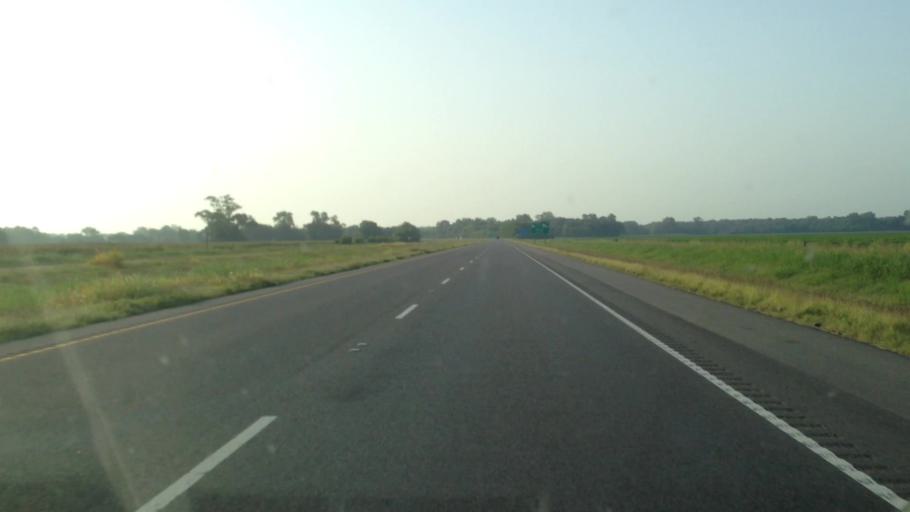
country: US
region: Louisiana
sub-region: Rapides Parish
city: Boyce
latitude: 31.3865
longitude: -92.6847
